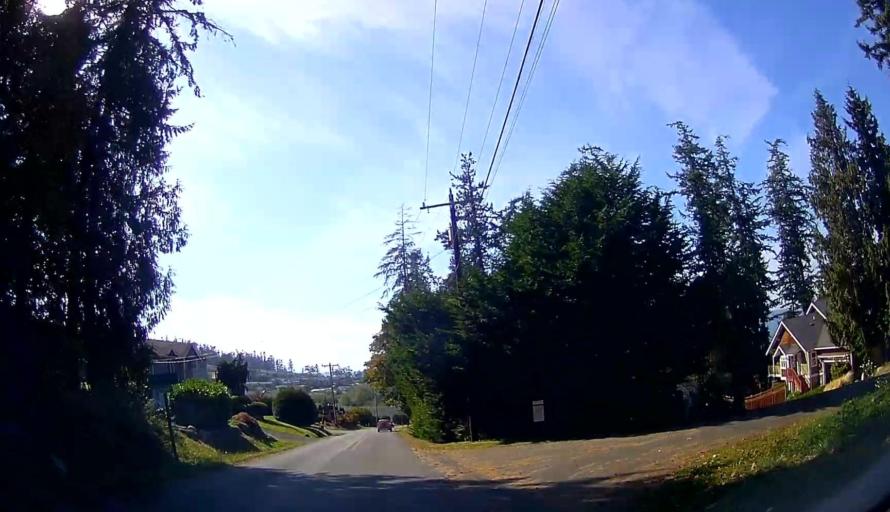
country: US
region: Washington
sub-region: Island County
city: Camano
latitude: 48.2482
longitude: -122.5206
